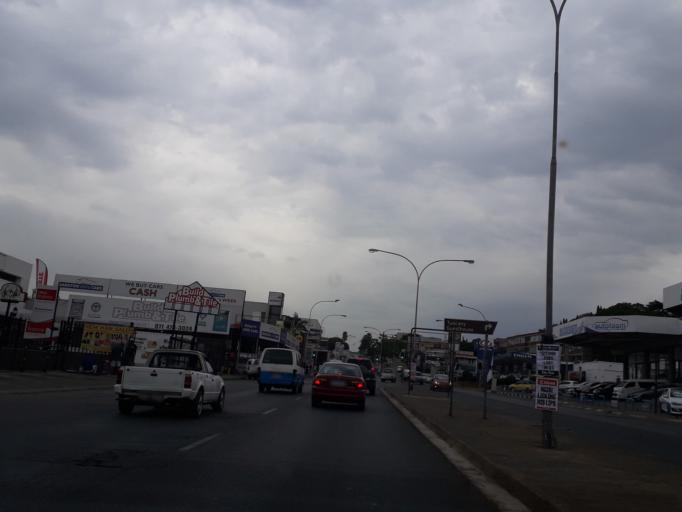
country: ZA
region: Gauteng
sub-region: City of Johannesburg Metropolitan Municipality
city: Johannesburg
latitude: -26.1342
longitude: 27.9744
